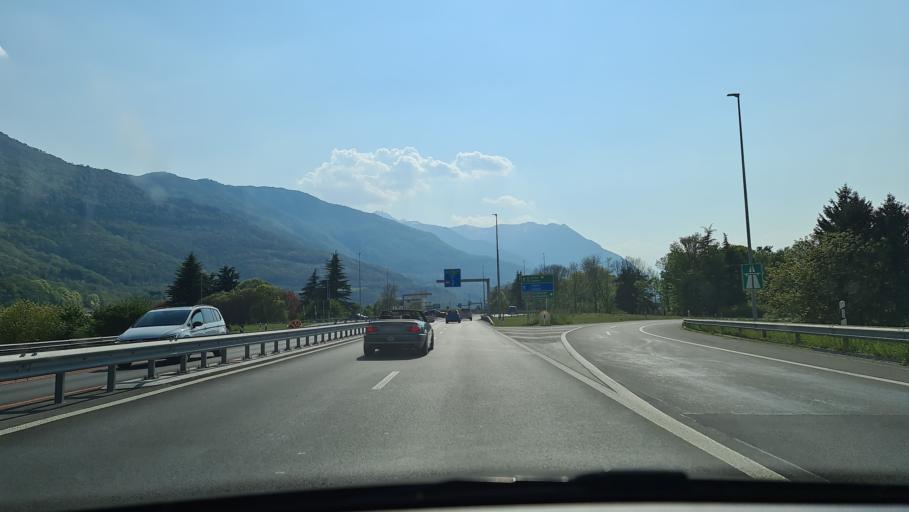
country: CH
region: Ticino
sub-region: Bellinzona District
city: Camorino
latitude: 46.1644
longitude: 8.9940
